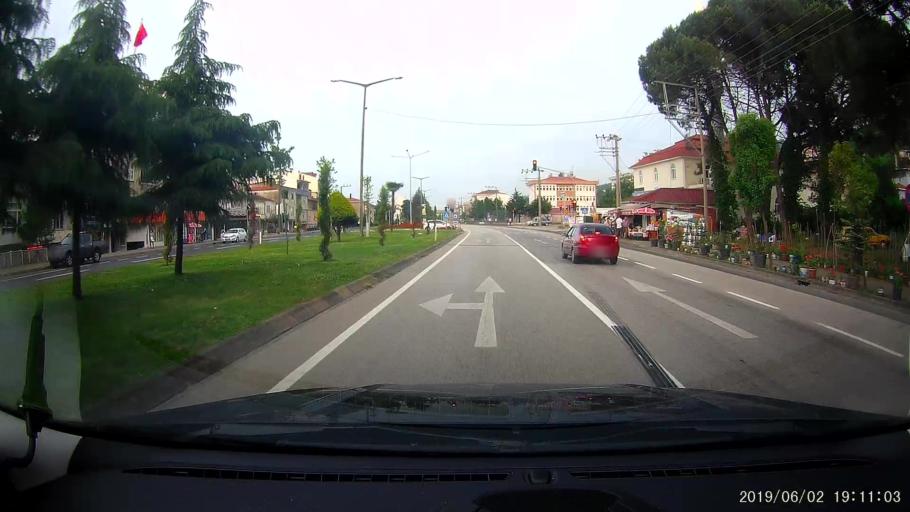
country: TR
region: Ordu
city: Gulyali
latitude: 40.9671
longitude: 38.0554
